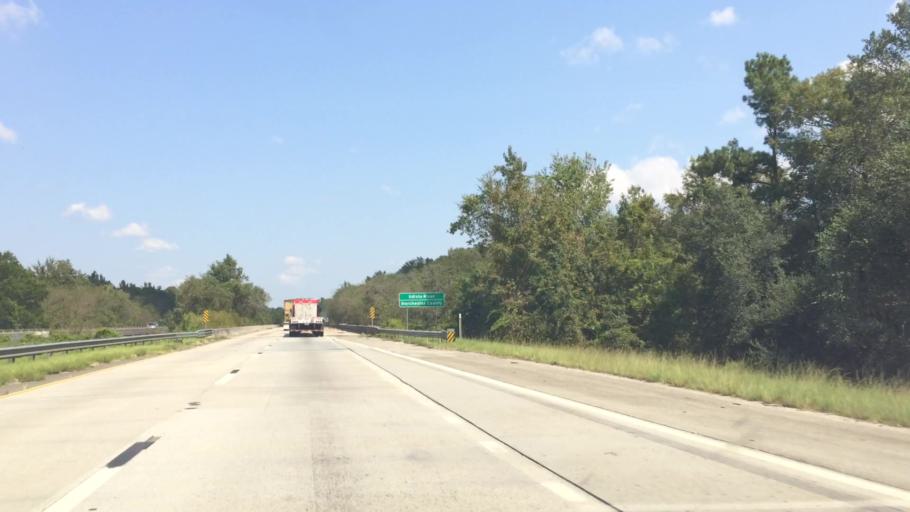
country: US
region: South Carolina
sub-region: Dorchester County
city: Saint George
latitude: 33.0892
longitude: -80.6502
